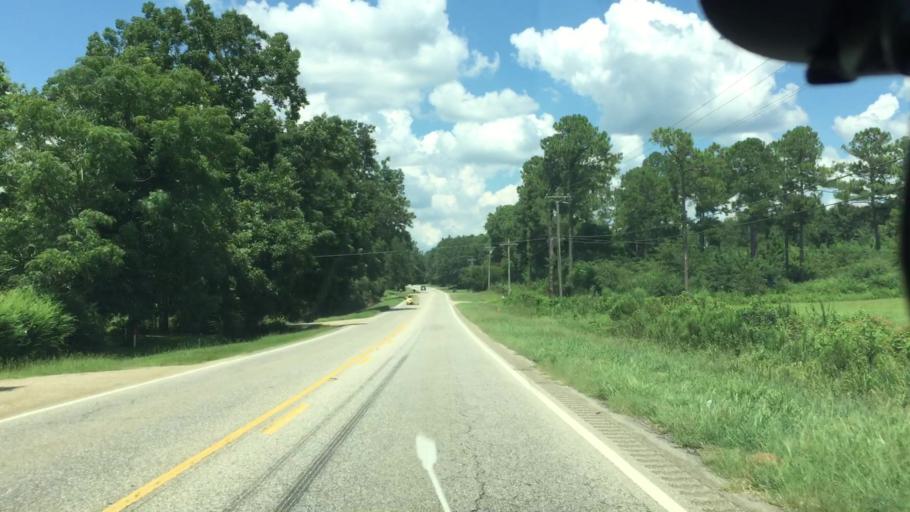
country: US
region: Alabama
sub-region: Pike County
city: Troy
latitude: 31.7239
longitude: -85.9592
